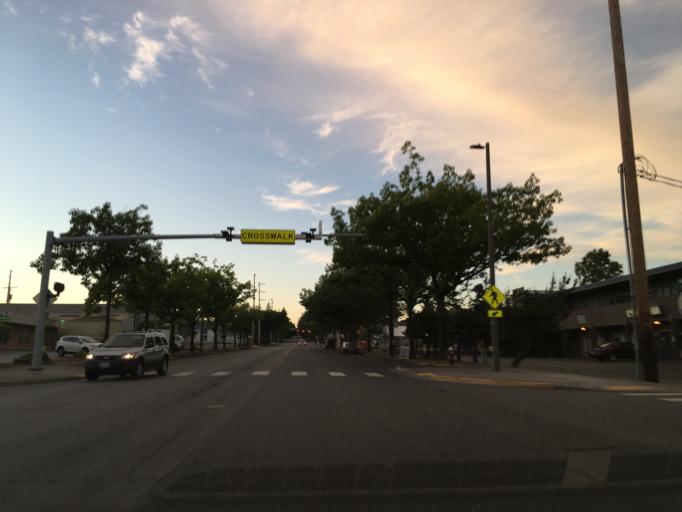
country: US
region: Washington
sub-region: Whatcom County
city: Bellingham
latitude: 48.7602
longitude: -122.4649
